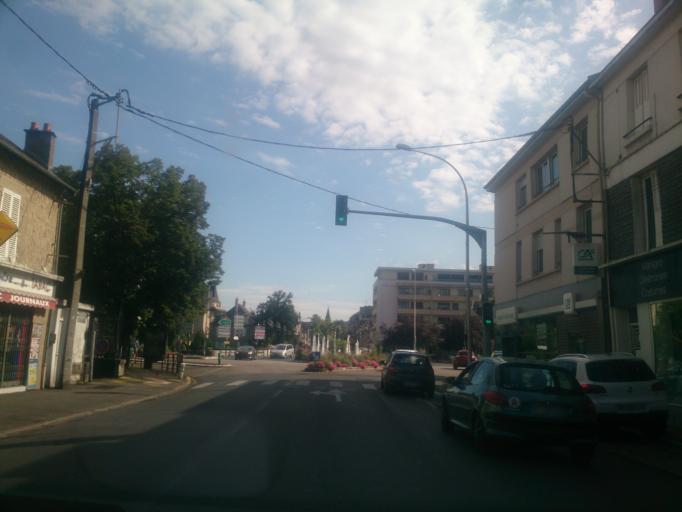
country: FR
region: Limousin
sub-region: Departement de la Correze
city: Brive-la-Gaillarde
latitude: 45.1657
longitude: 1.5319
